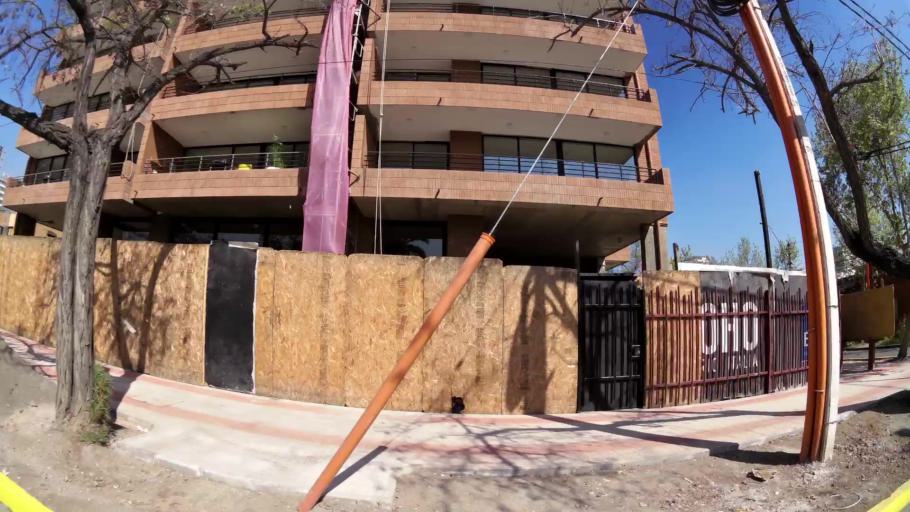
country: CL
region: Santiago Metropolitan
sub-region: Provincia de Santiago
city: Santiago
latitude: -33.4493
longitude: -70.6227
